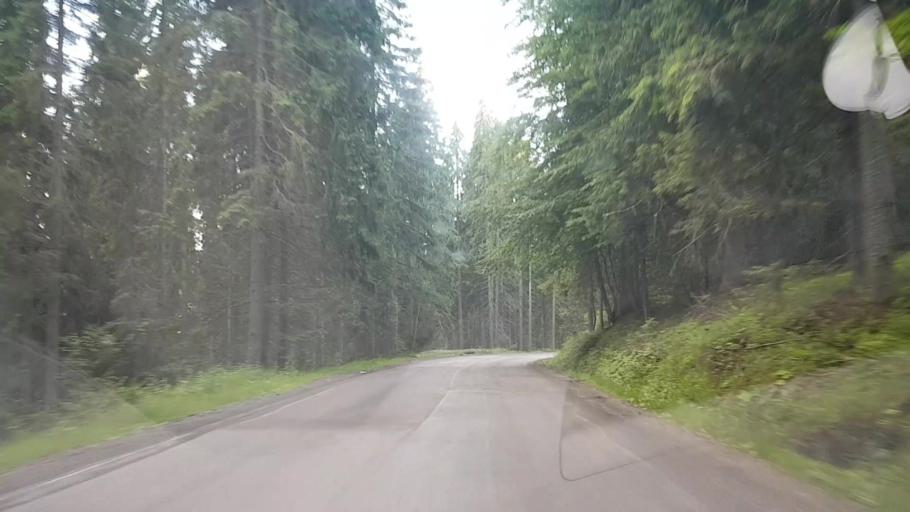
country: RO
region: Harghita
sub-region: Comuna Varsag
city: Varsag
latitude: 46.6507
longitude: 25.2899
